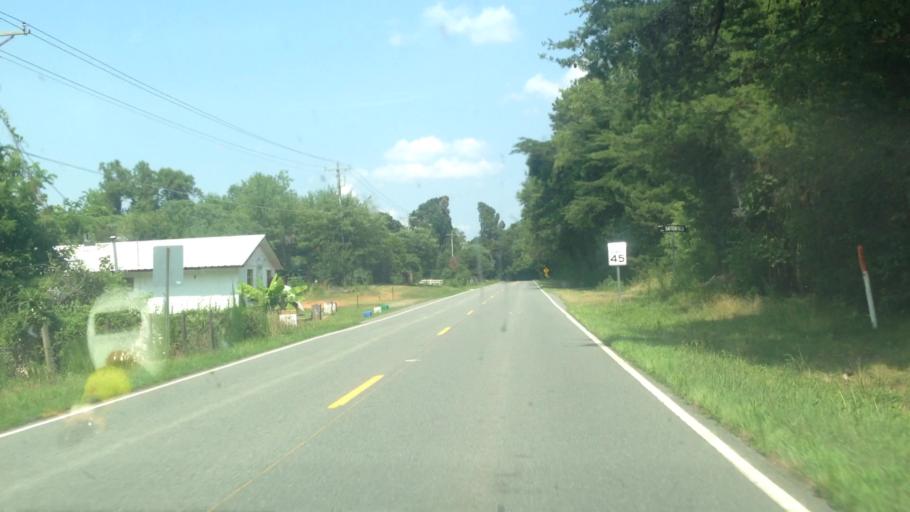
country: US
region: North Carolina
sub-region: Stokes County
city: Walnut Cove
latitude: 36.3053
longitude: -80.0507
